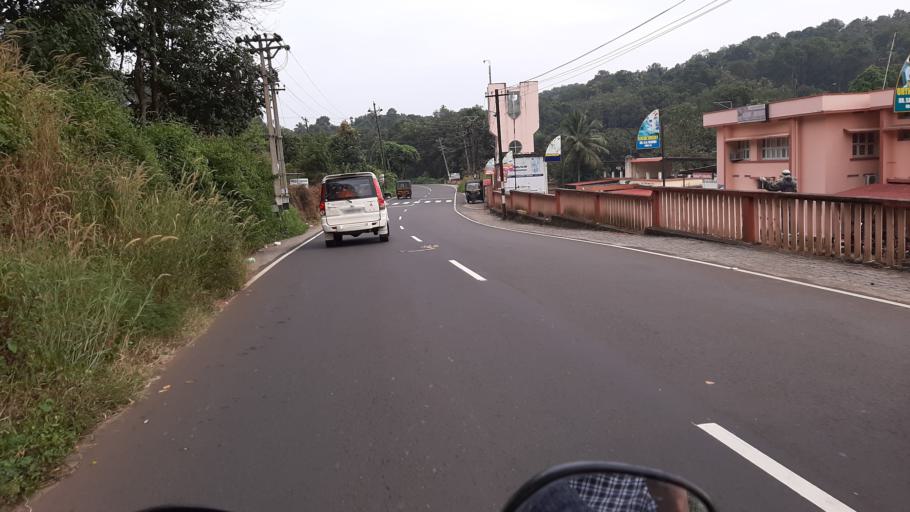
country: IN
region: Kerala
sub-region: Pattanamtitta
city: Pathanamthitta
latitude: 9.4491
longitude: 76.8719
